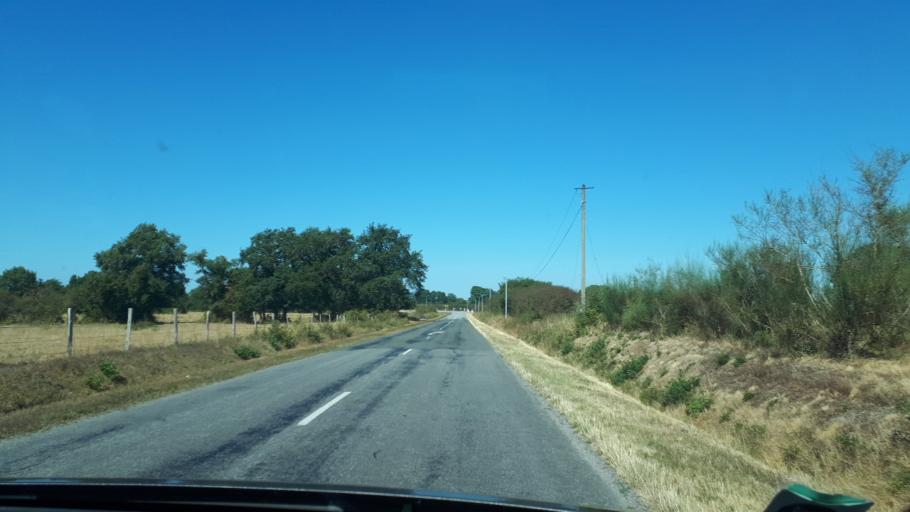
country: FR
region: Centre
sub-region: Departement du Loiret
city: Coullons
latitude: 47.6368
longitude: 2.4482
